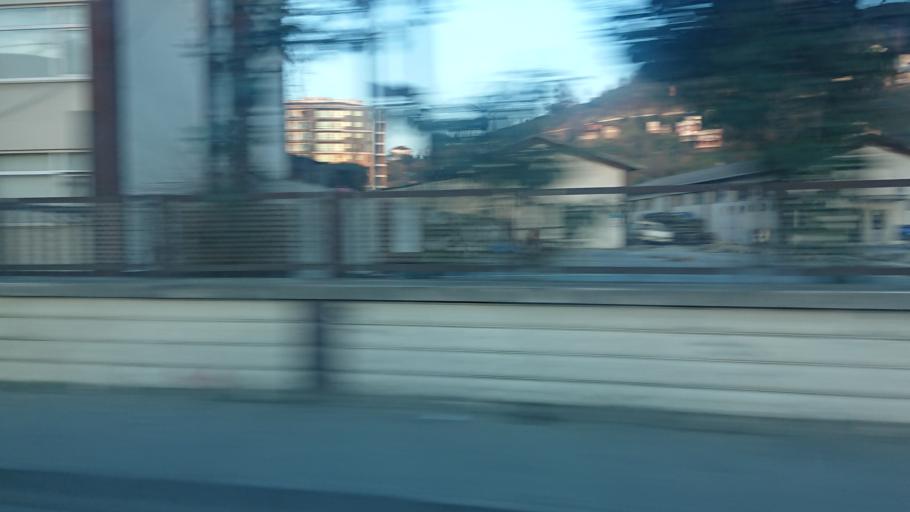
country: TR
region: Rize
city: Gundogdu
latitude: 41.0408
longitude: 40.5793
